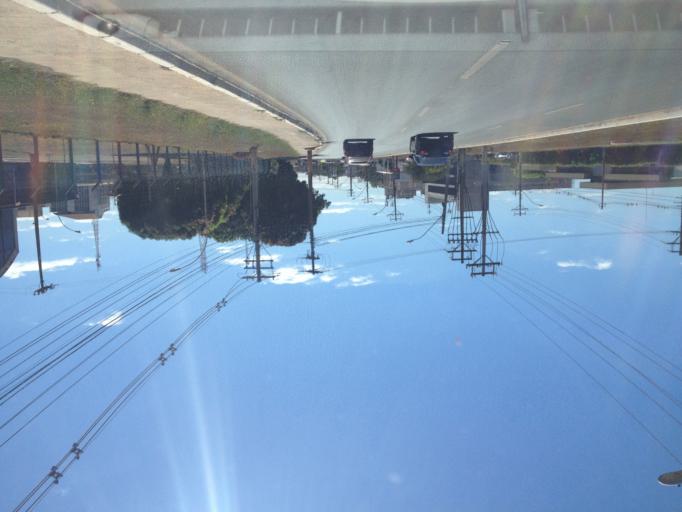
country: BR
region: Federal District
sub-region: Brasilia
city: Brasilia
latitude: -15.8013
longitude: -47.9504
